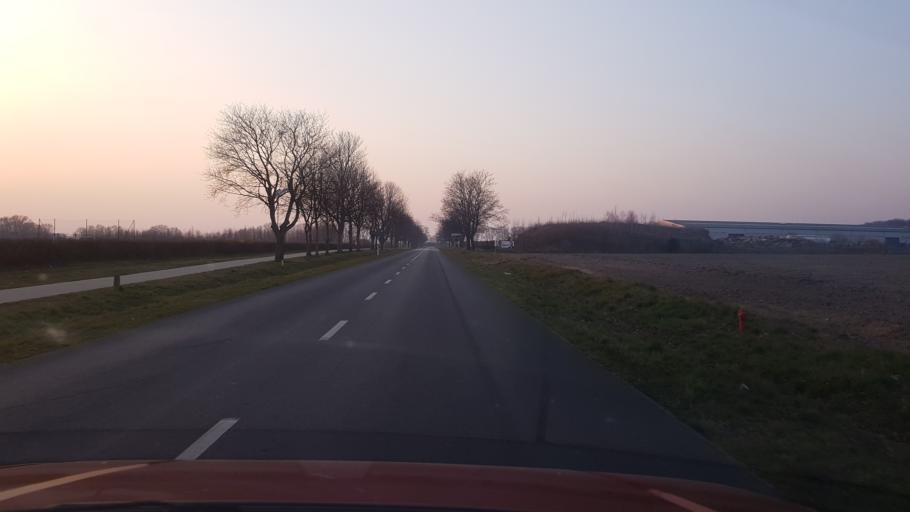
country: PL
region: West Pomeranian Voivodeship
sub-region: Powiat lobeski
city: Radowo Male
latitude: 53.6692
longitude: 15.4425
